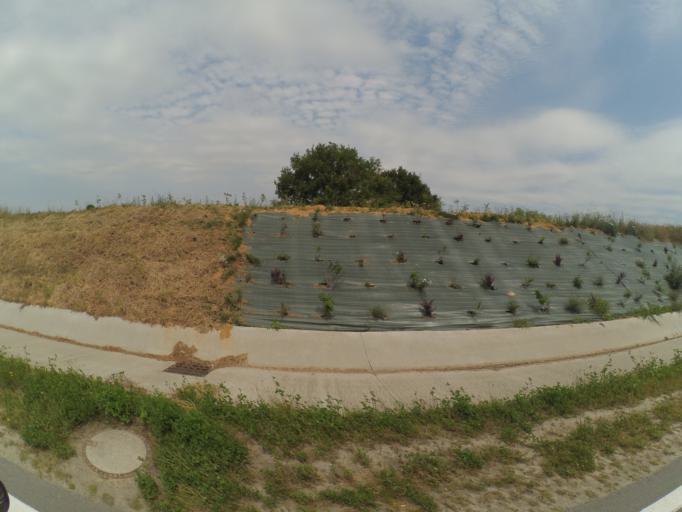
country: FR
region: Pays de la Loire
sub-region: Departement de la Vendee
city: Saint-Paul-en-Pareds
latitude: 46.8444
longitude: -0.9956
